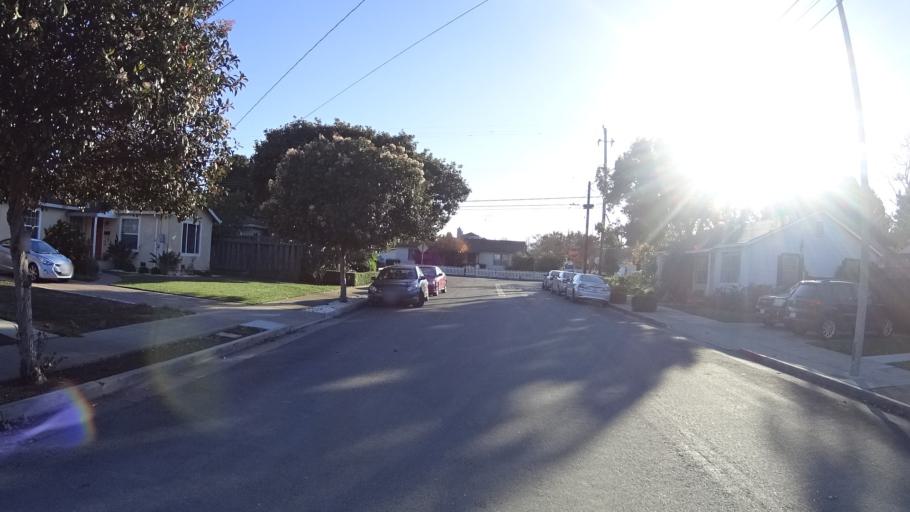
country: US
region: California
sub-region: Santa Clara County
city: Sunnyvale
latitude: 37.3817
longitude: -122.0284
